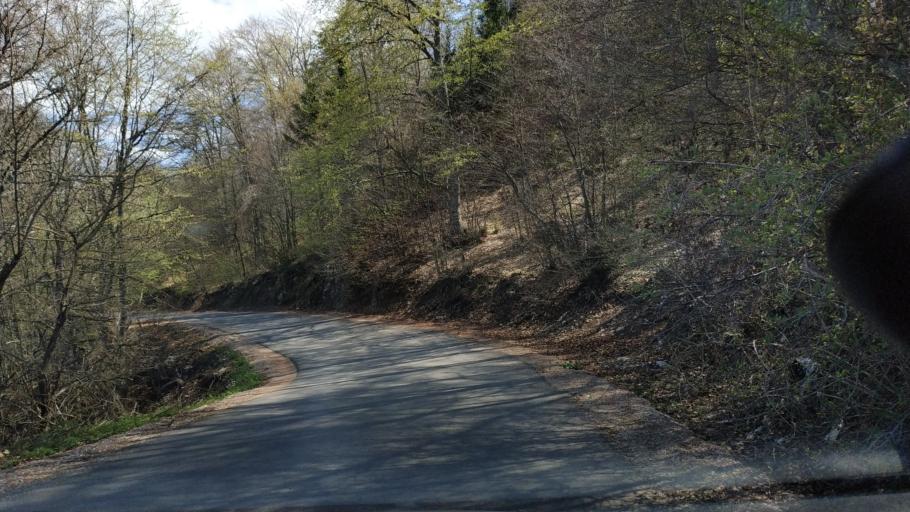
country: RS
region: Central Serbia
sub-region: Zajecarski Okrug
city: Soko Banja
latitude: 43.5852
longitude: 21.8889
